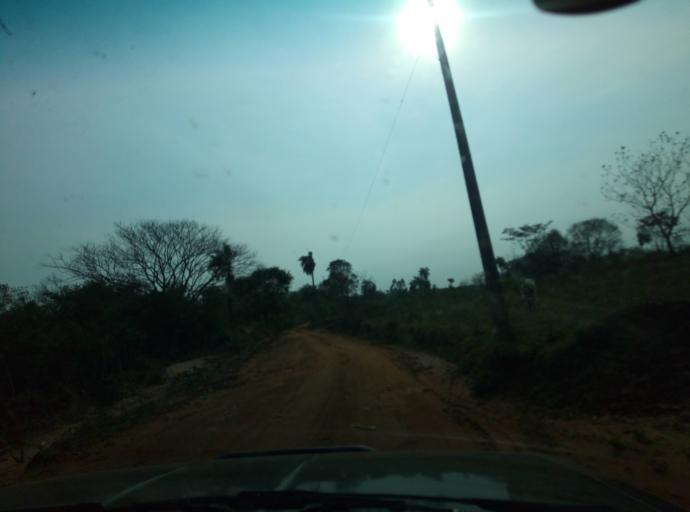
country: PY
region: Caaguazu
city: San Joaquin
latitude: -25.1520
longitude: -56.1047
